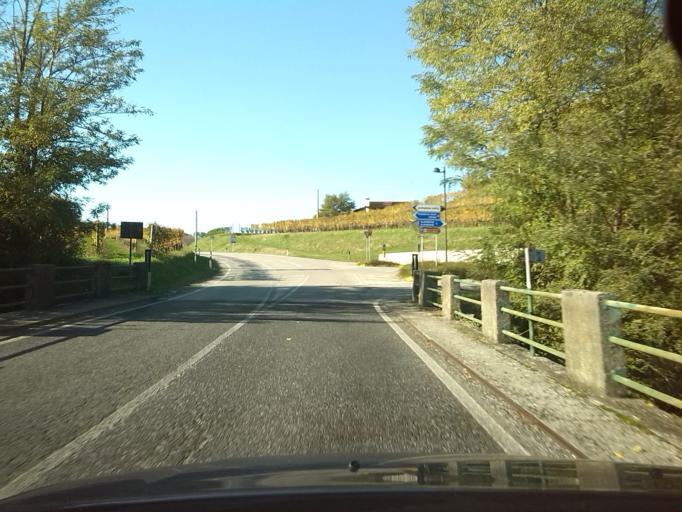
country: IT
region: Friuli Venezia Giulia
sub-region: Provincia di Udine
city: Corno di Rosazzo
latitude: 46.0031
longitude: 13.4685
